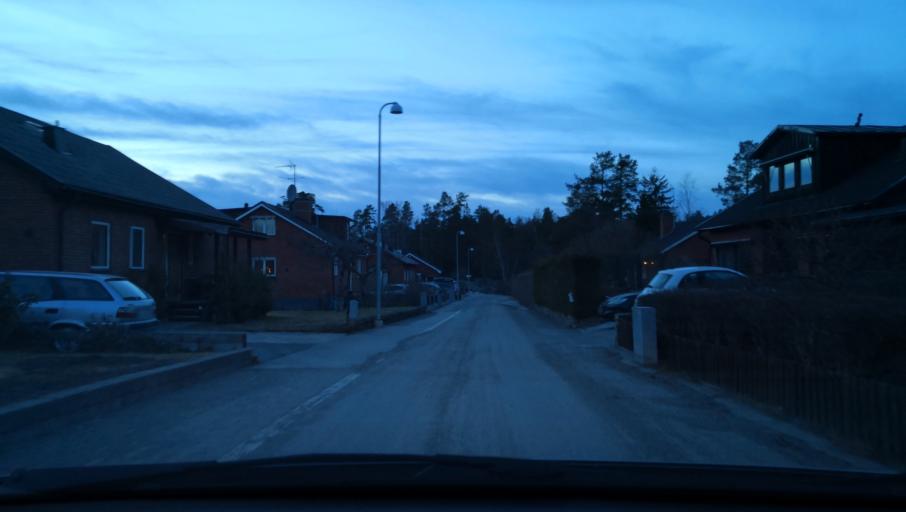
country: SE
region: Stockholm
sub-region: Varmdo Kommun
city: Gustavsberg
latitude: 59.3376
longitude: 18.3865
